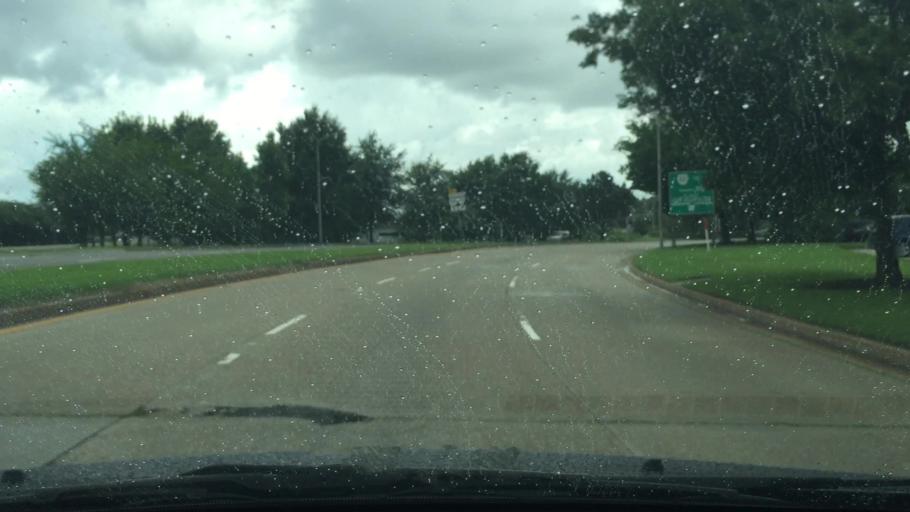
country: US
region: Virginia
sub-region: City of Norfolk
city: Norfolk
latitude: 36.8606
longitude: -76.3067
